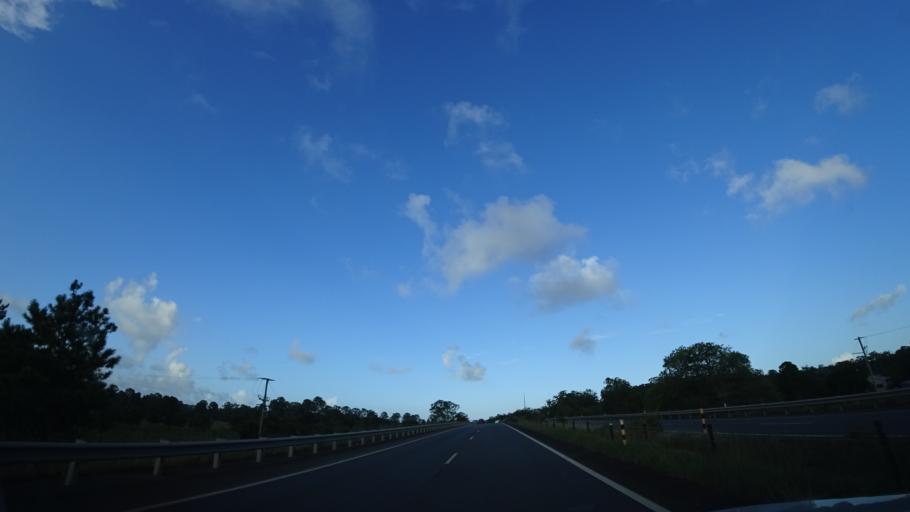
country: AU
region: Queensland
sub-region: Sunshine Coast
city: Buderim
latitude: -26.6689
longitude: 153.0204
